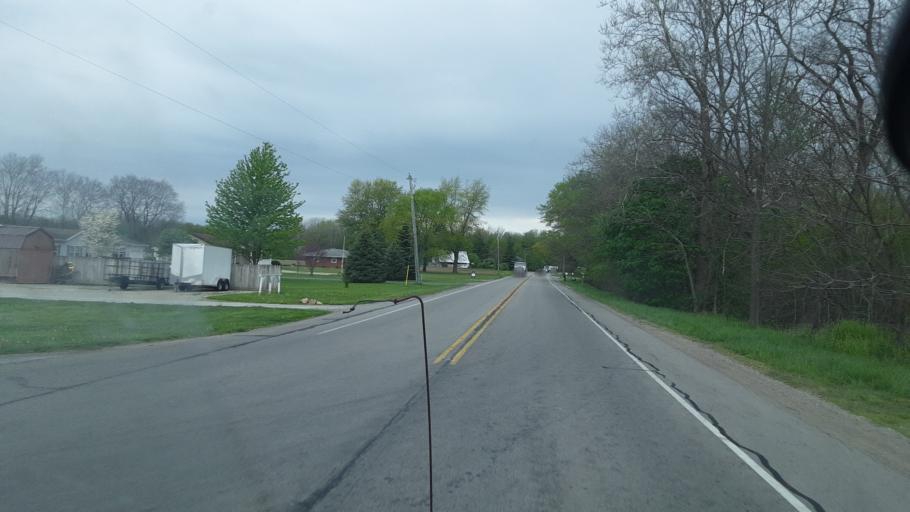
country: US
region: Indiana
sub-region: Elkhart County
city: New Paris
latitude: 41.5046
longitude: -85.7517
